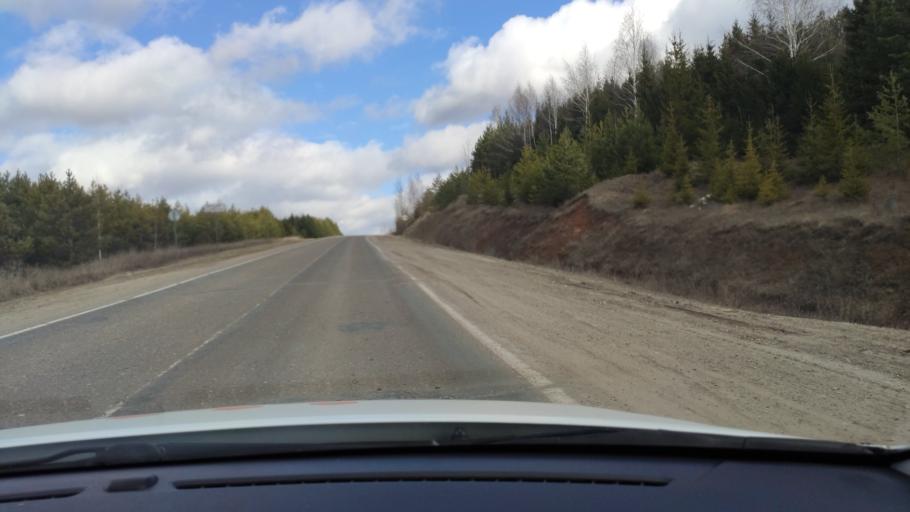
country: RU
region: Tatarstan
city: Vysokaya Gora
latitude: 56.1302
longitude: 49.2125
